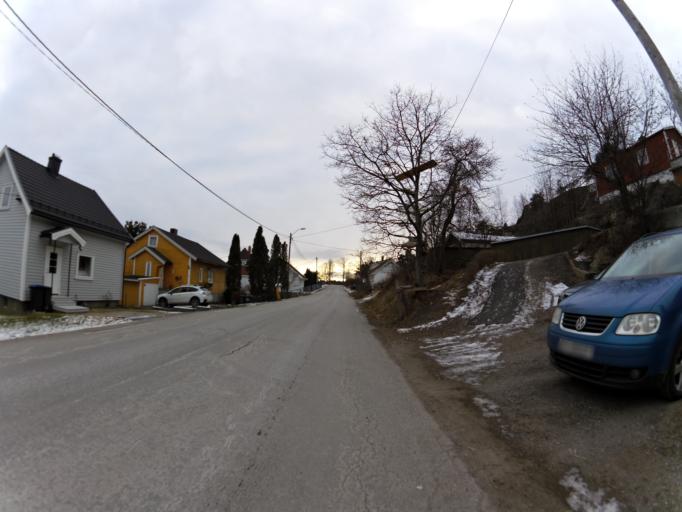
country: NO
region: Ostfold
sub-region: Fredrikstad
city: Fredrikstad
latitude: 59.2097
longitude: 10.8872
